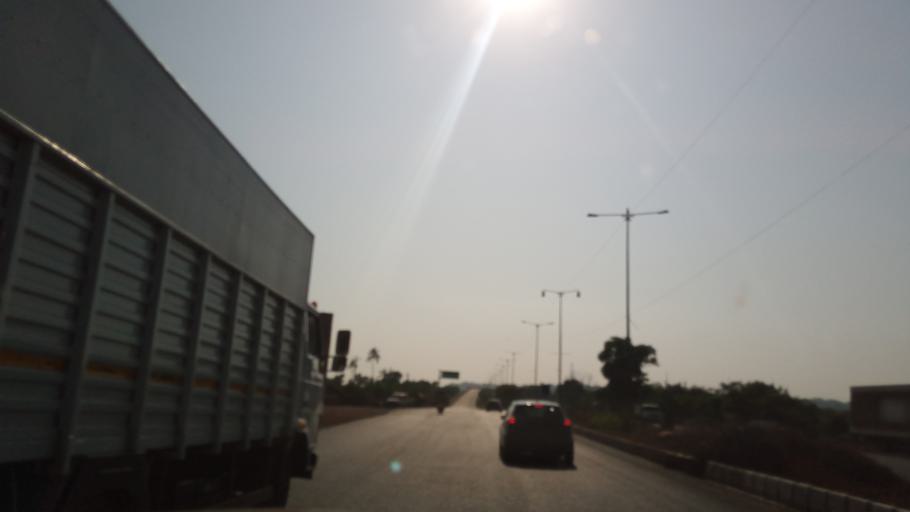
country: IN
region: Goa
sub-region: North Goa
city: Panaji
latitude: 15.4934
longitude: 73.8492
